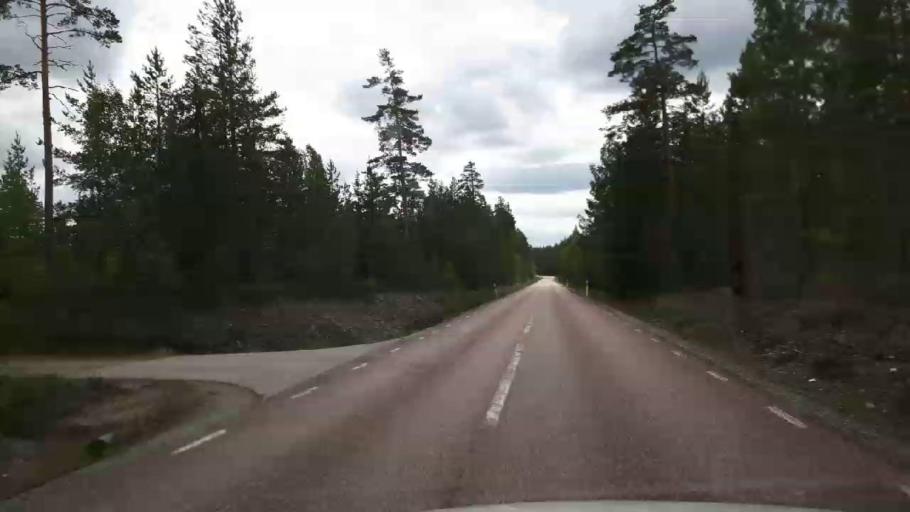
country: SE
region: Vaestmanland
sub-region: Fagersta Kommun
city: Fagersta
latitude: 59.8673
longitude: 15.8422
